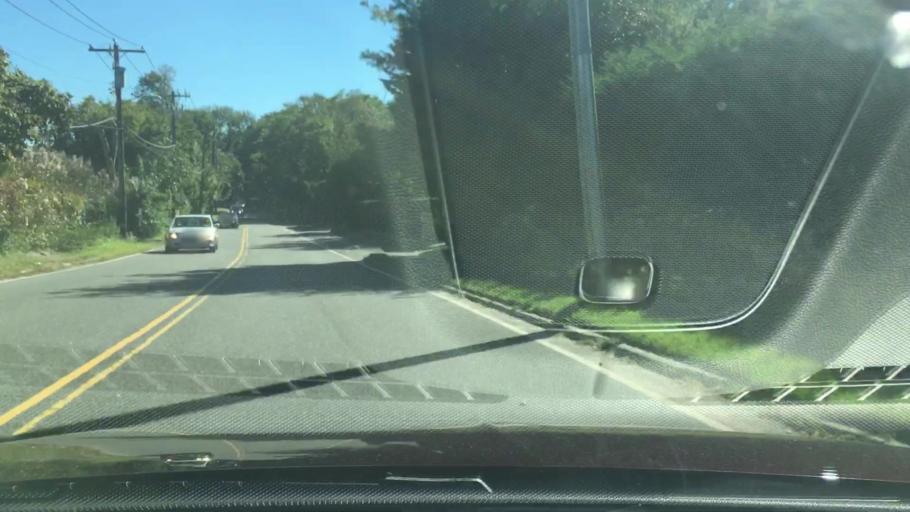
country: US
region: New York
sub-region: Nassau County
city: Plandome
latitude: 40.8138
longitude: -73.7036
